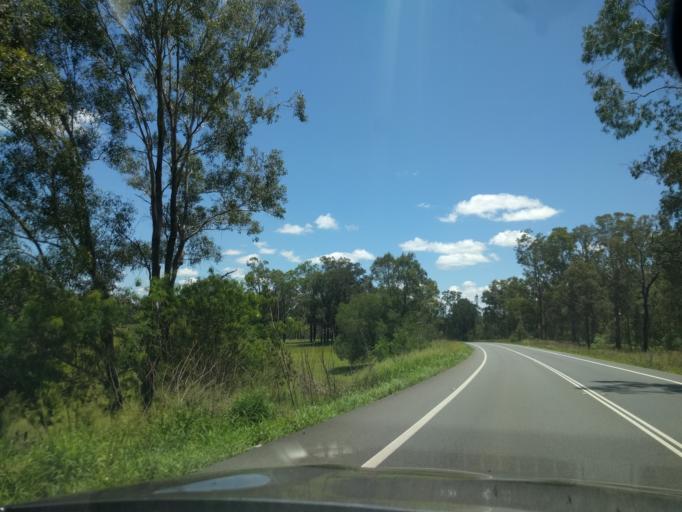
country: AU
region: Queensland
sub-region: Logan
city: Cedar Vale
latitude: -27.8723
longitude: 152.9962
